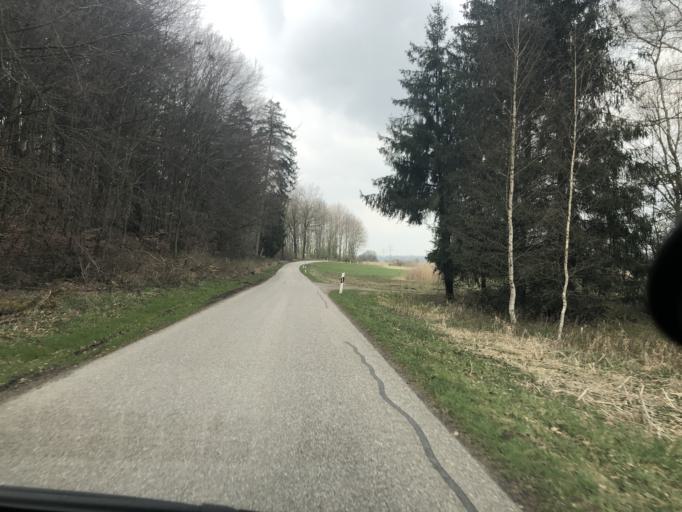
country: DE
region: Bavaria
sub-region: Upper Bavaria
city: Wolfersdorf
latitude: 48.4424
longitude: 11.7057
